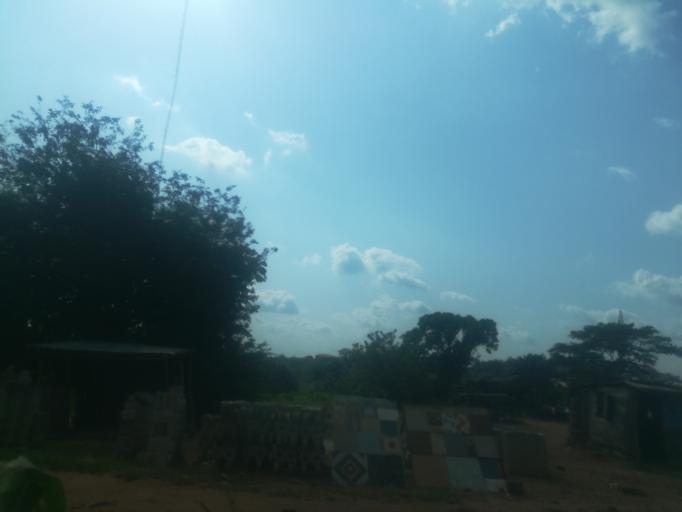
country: NG
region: Oyo
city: Moniya
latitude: 7.5239
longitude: 3.9118
